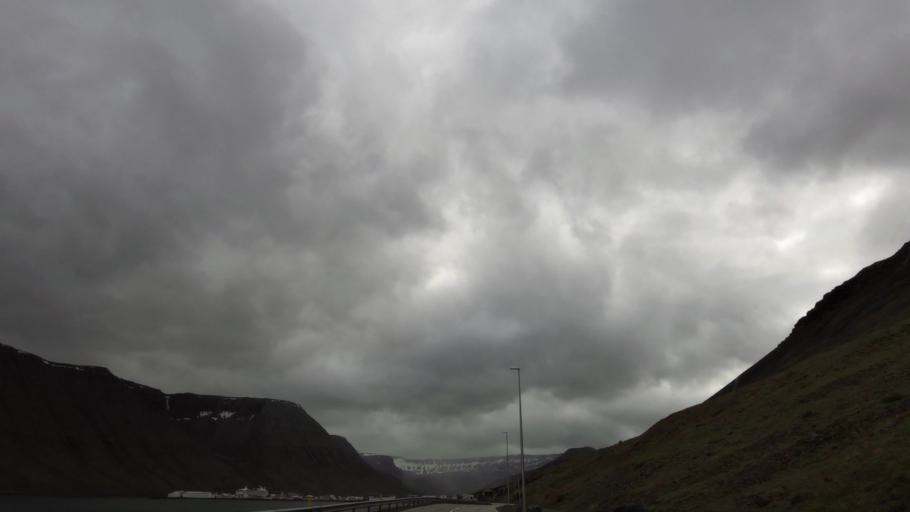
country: IS
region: Westfjords
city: Isafjoerdur
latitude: 66.0882
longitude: -23.1171
